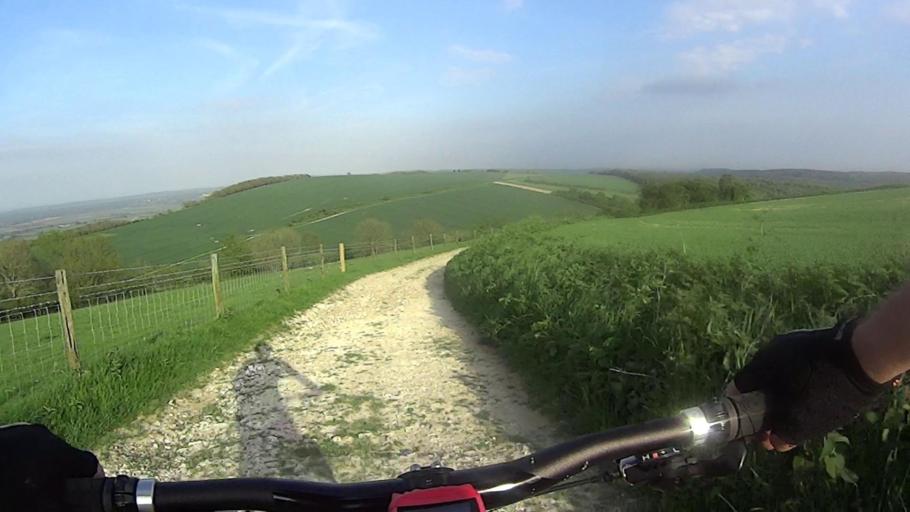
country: GB
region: England
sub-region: West Sussex
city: Walberton
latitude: 50.9090
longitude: -0.5980
